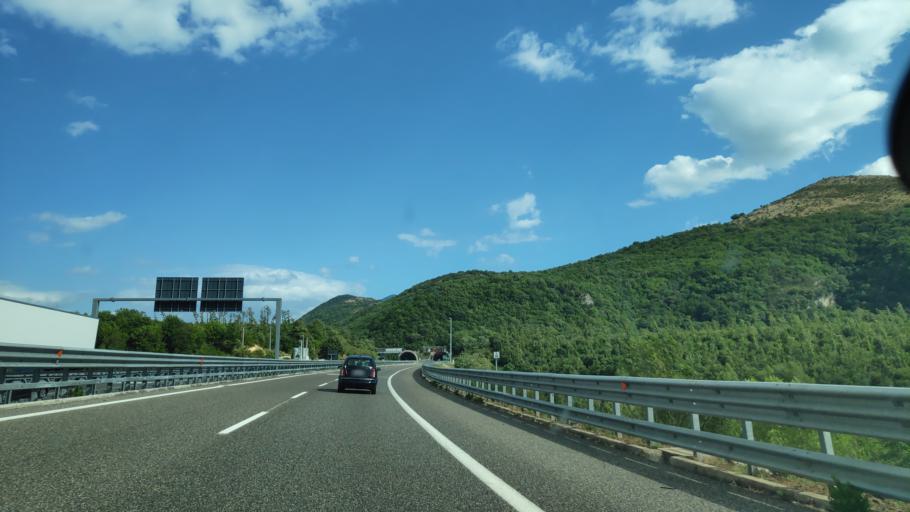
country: IT
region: Campania
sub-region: Provincia di Salerno
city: Sicignano degli Alburni
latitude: 40.6085
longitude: 15.2968
